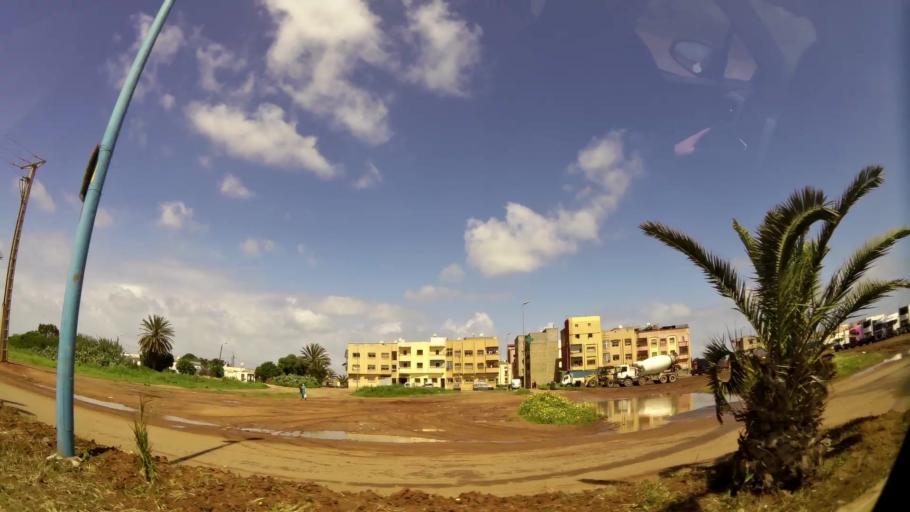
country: MA
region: Grand Casablanca
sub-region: Mediouna
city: Tit Mellil
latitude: 33.6362
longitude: -7.4594
